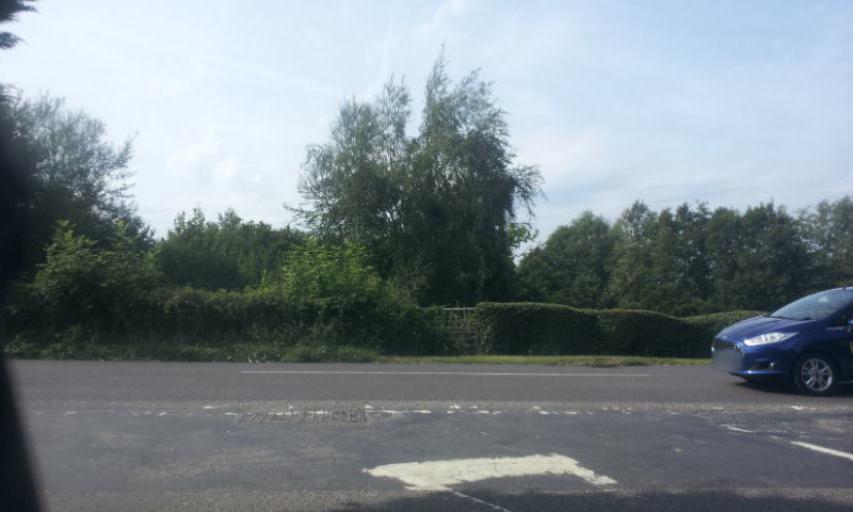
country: GB
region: England
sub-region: Kent
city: Paddock Wood
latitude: 51.1662
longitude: 0.3855
